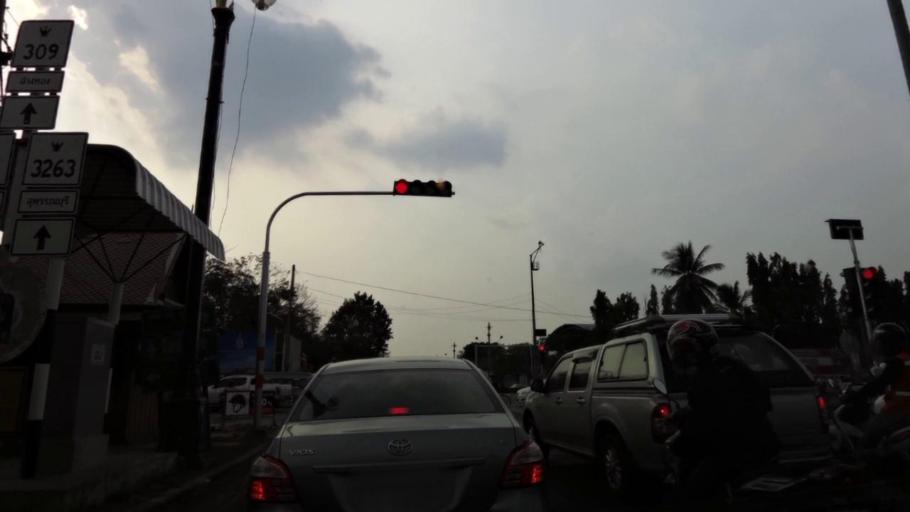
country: TH
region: Phra Nakhon Si Ayutthaya
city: Phra Nakhon Si Ayutthaya
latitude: 14.3501
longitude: 100.5748
